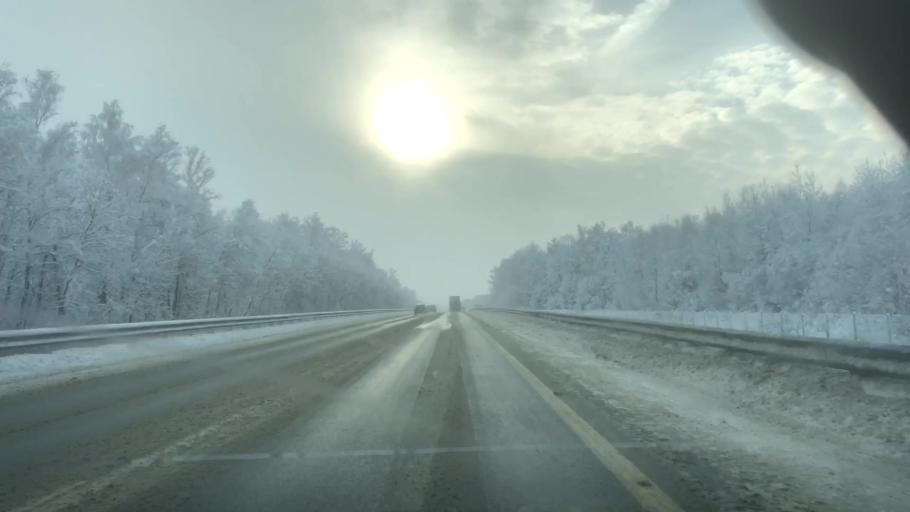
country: RU
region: Tula
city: Venev
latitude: 54.5259
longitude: 38.1680
